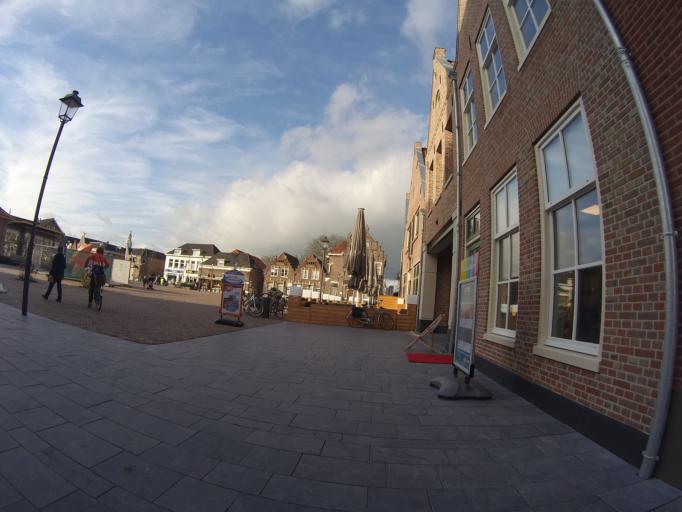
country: NL
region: Gelderland
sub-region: Gemeente Nijkerk
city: Nijkerk
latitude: 52.2235
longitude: 5.4890
